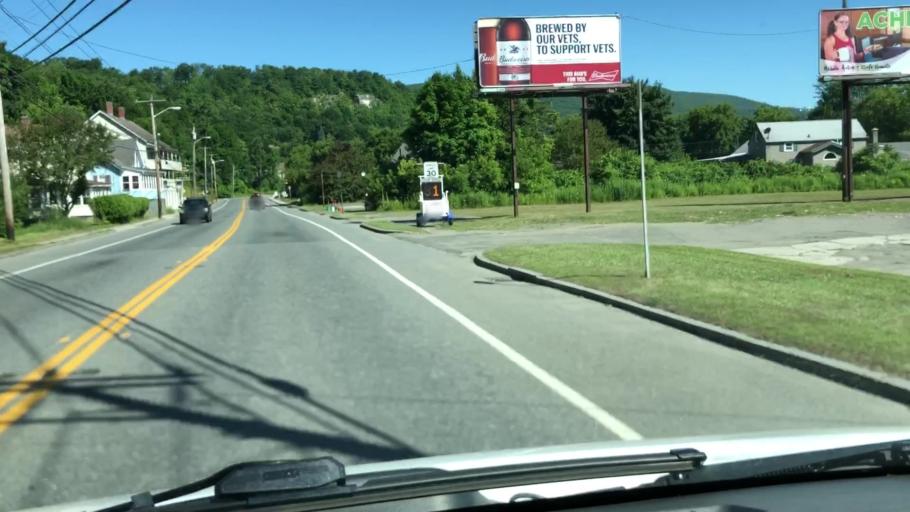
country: US
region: Massachusetts
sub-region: Berkshire County
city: North Adams
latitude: 42.6894
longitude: -73.1121
